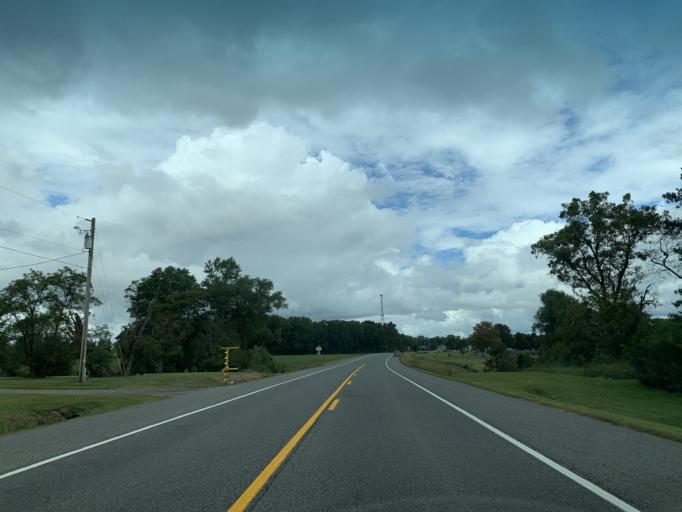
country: US
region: Maryland
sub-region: Caroline County
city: Denton
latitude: 38.8865
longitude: -75.8455
